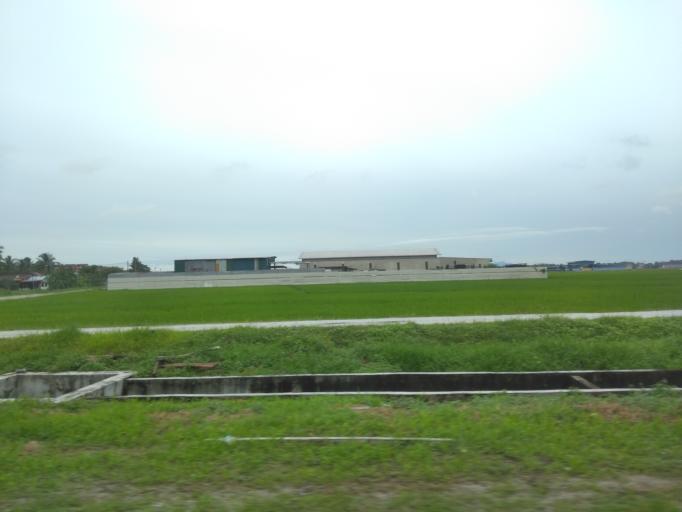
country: MY
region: Penang
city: Perai
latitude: 5.4109
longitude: 100.4178
